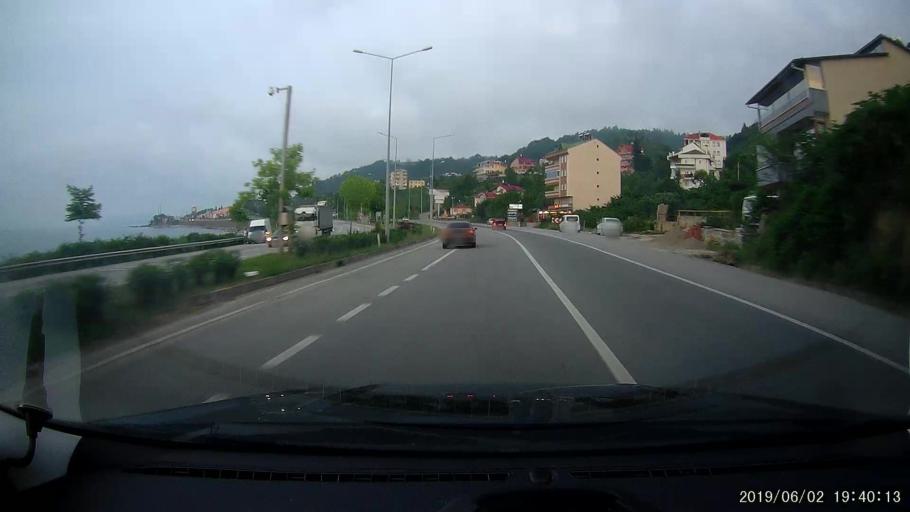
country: TR
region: Giresun
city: Kesap
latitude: 40.9149
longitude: 38.4550
